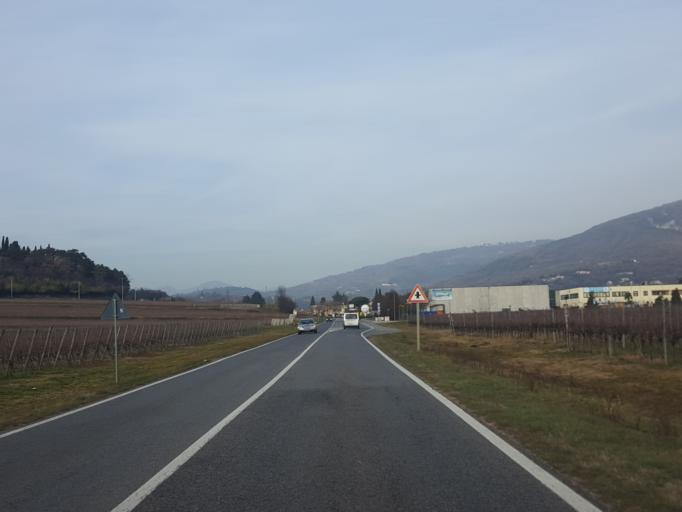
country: IT
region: Veneto
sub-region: Provincia di Verona
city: Costermano
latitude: 45.5810
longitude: 10.7541
